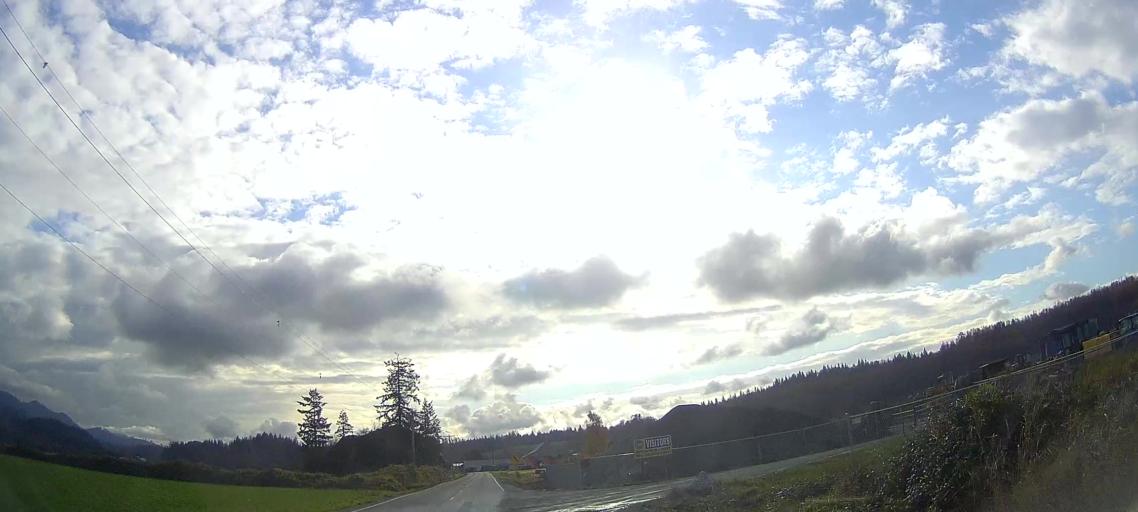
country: US
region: Washington
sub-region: Skagit County
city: Clear Lake
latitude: 48.4359
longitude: -122.2210
